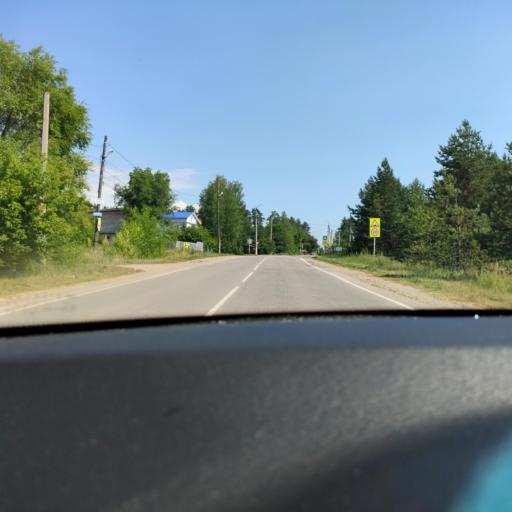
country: RU
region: Samara
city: Volzhskiy
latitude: 53.4534
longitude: 50.1701
